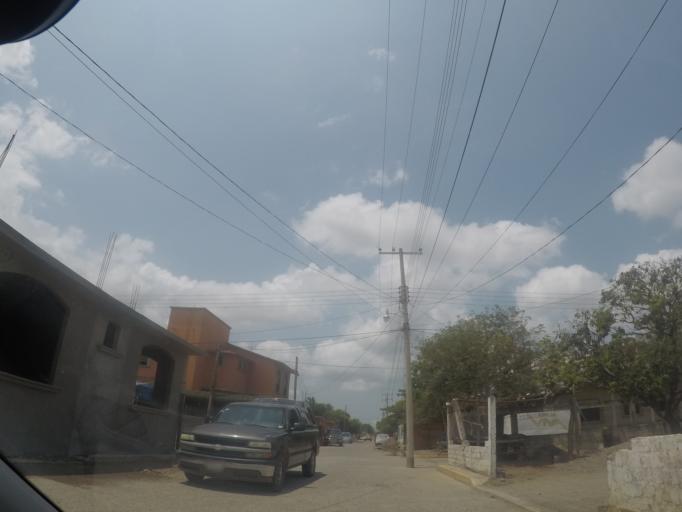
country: MX
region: Oaxaca
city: El Espinal
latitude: 16.5522
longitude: -94.9484
